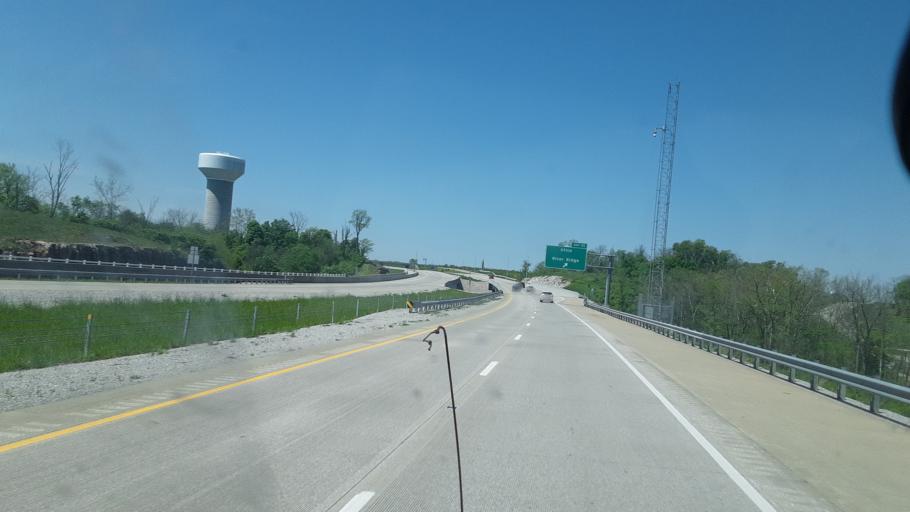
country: US
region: Kentucky
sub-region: Jefferson County
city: Prospect
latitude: 38.3500
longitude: -85.6571
